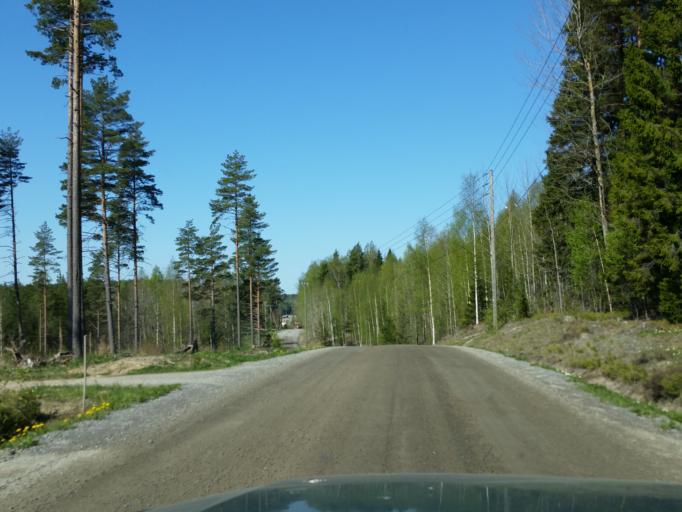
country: FI
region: Uusimaa
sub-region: Helsinki
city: Karjalohja
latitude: 60.1451
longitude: 23.8082
